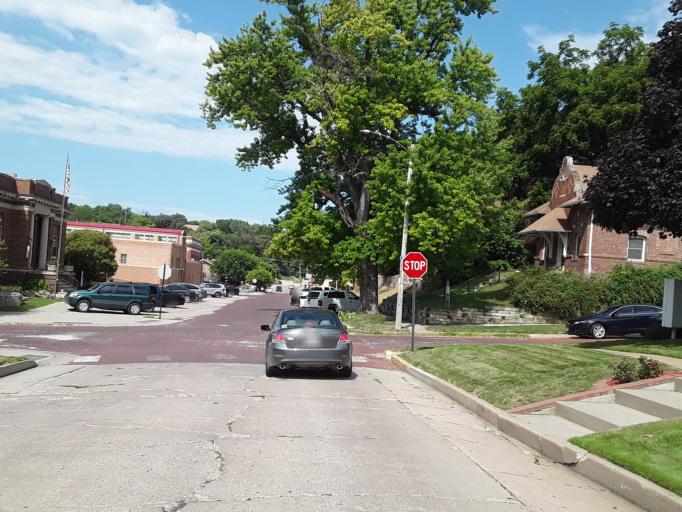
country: US
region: Nebraska
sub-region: Cass County
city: Plattsmouth
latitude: 41.0122
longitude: -95.8834
